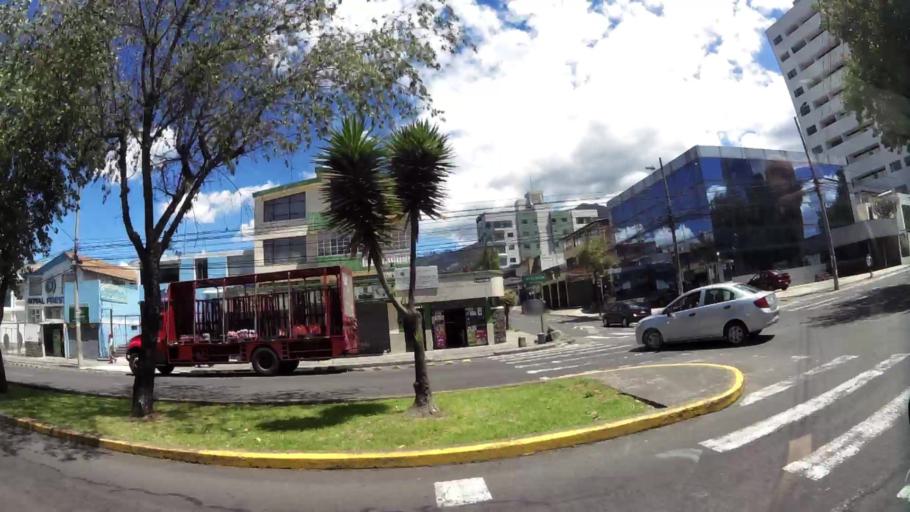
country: EC
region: Pichincha
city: Quito
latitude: -0.1799
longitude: -78.4911
